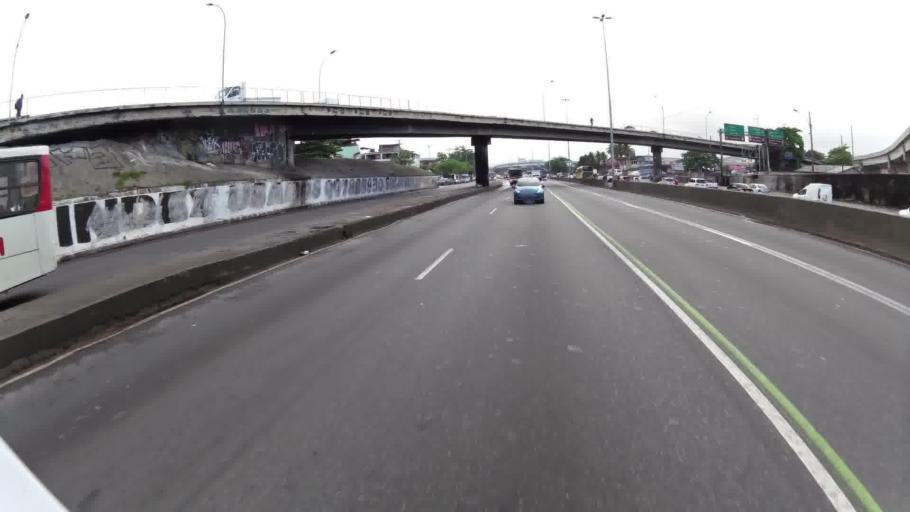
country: BR
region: Rio de Janeiro
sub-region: Rio De Janeiro
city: Rio de Janeiro
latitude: -22.8501
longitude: -43.2472
